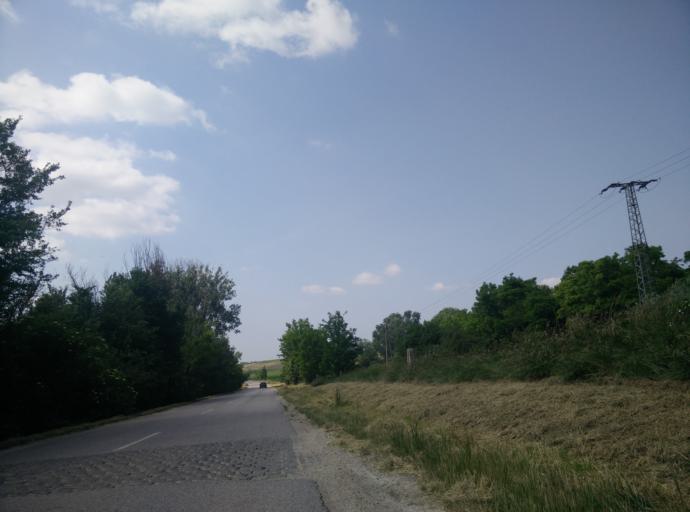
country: HU
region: Pest
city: Biatorbagy
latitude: 47.4701
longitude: 18.8032
